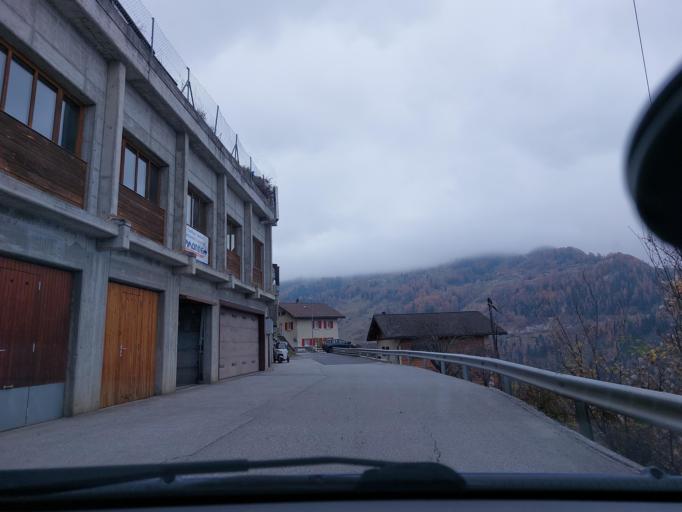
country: CH
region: Valais
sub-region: Martigny District
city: Riddes
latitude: 46.1672
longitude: 7.2438
